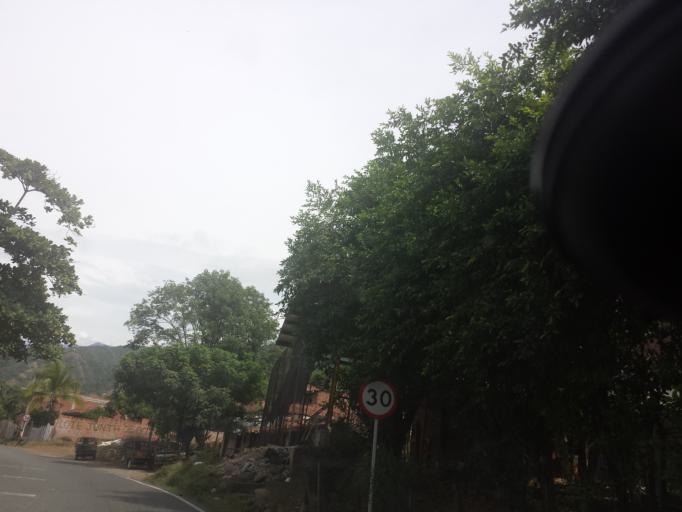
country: CO
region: Antioquia
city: Antioquia
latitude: 6.5625
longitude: -75.8326
